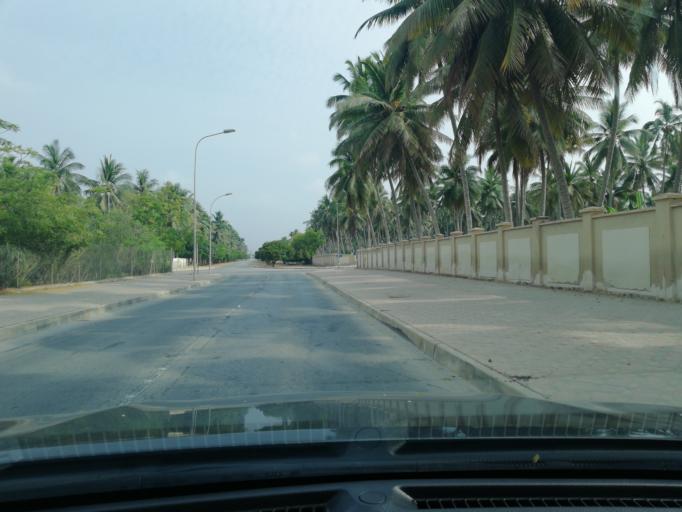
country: OM
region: Zufar
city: Salalah
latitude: 17.0126
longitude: 54.1468
